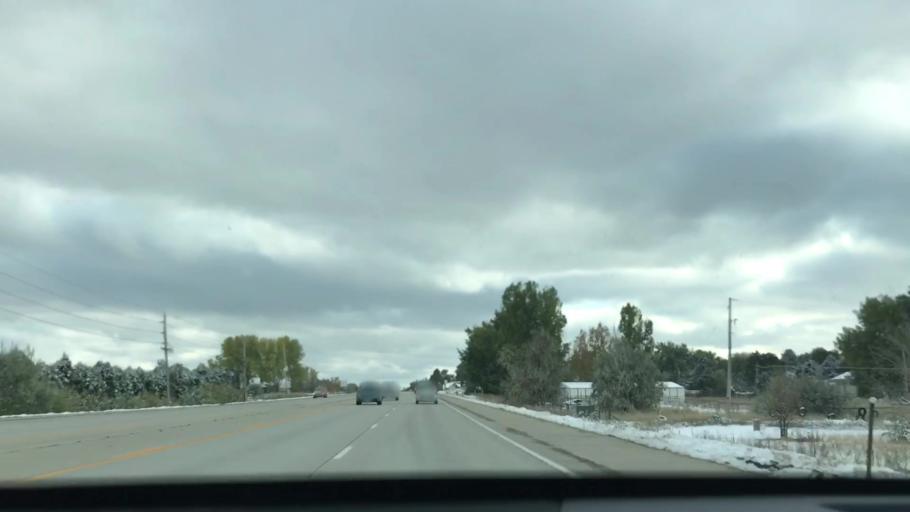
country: US
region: Colorado
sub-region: Boulder County
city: Lafayette
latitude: 40.0225
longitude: -105.1028
